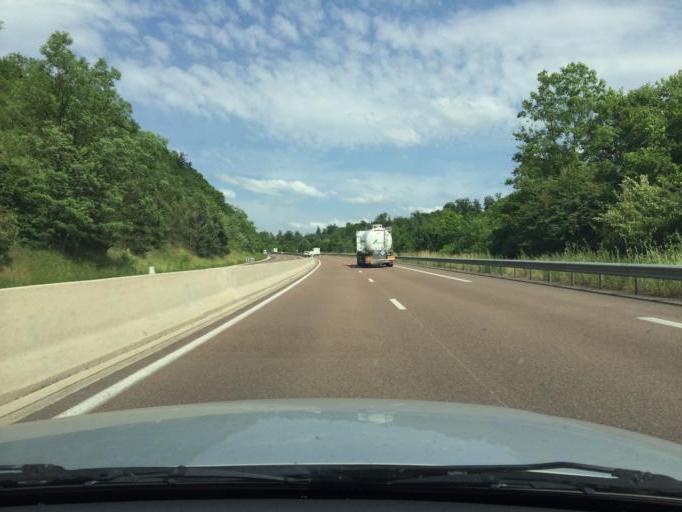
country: FR
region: Lorraine
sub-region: Departement de la Meuse
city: Ligny-en-Barrois
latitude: 48.6928
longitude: 5.3400
